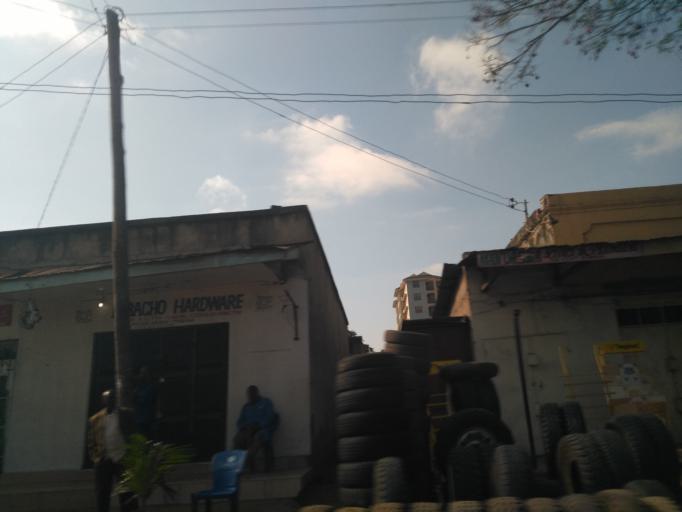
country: TZ
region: Arusha
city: Arusha
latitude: -3.3724
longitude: 36.6835
